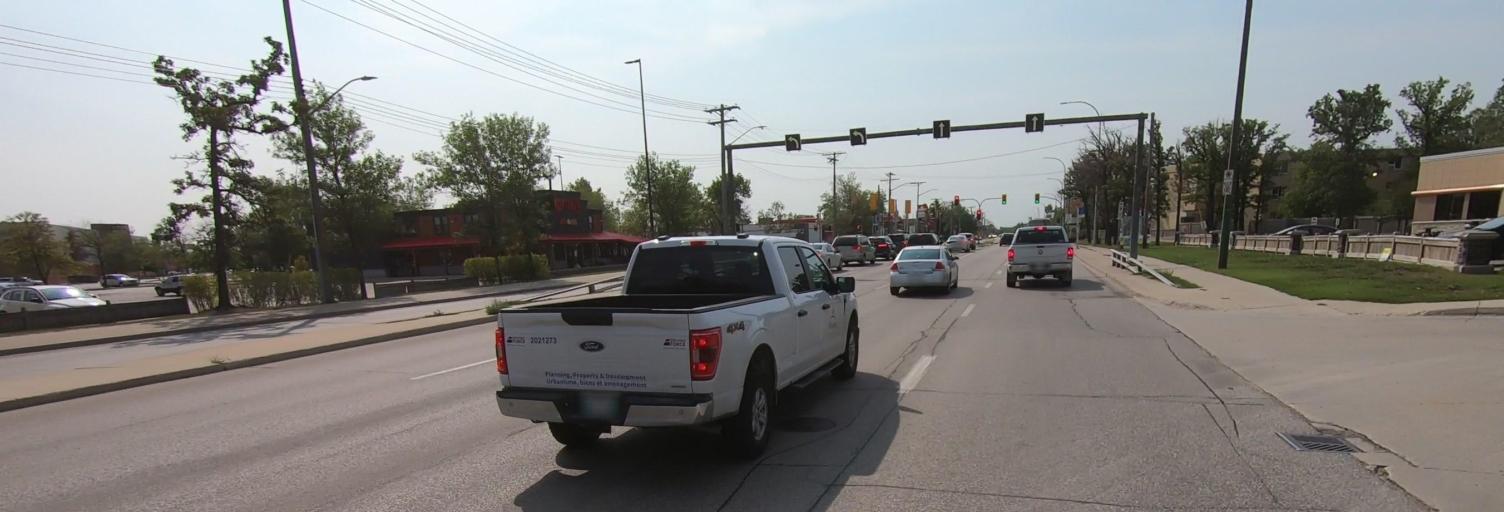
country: CA
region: Manitoba
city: Winnipeg
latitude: 49.8288
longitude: -97.1146
